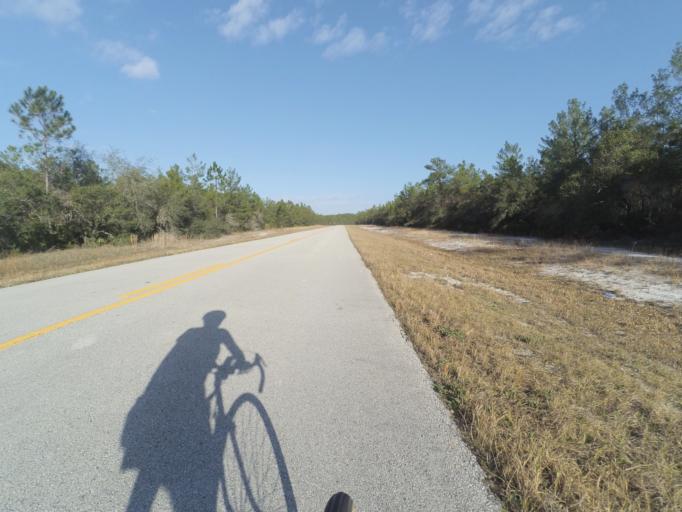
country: US
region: Florida
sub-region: Lake County
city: Astor
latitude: 29.1234
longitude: -81.5776
